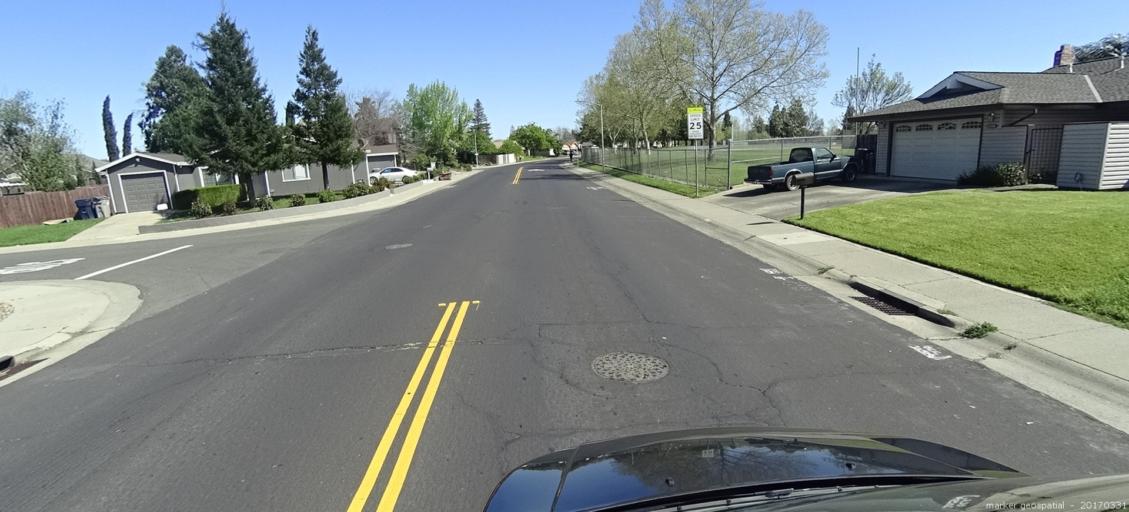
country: US
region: California
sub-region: Sacramento County
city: Laguna
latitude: 38.4570
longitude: -121.4327
